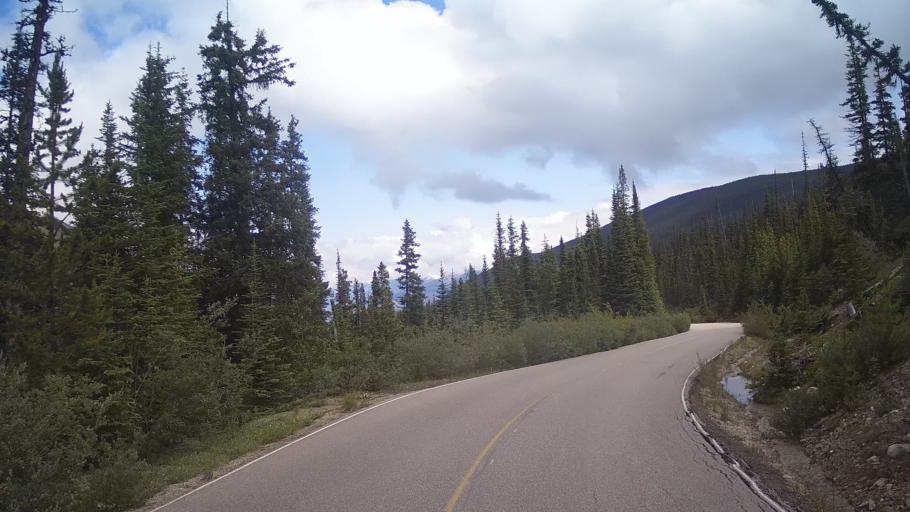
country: CA
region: Alberta
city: Jasper Park Lodge
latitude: 52.7080
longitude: -118.0573
